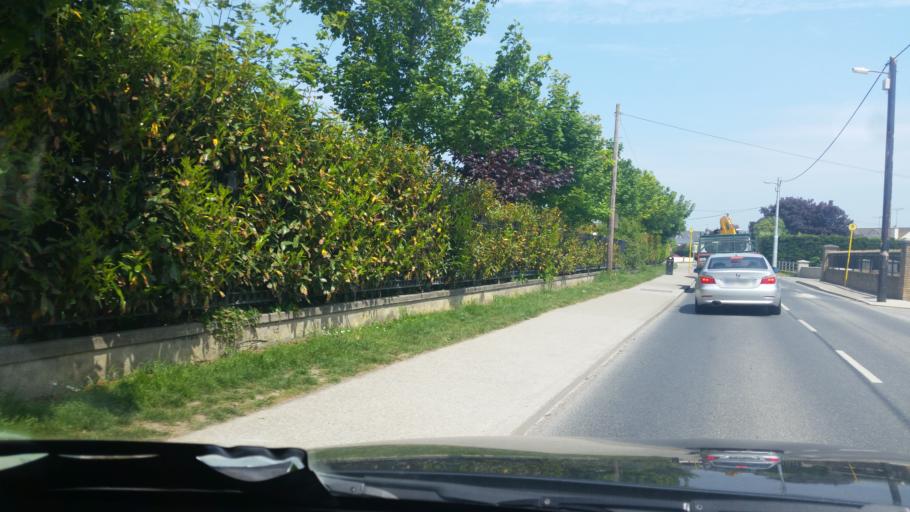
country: IE
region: Leinster
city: Donabate
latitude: 53.4910
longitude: -6.1397
